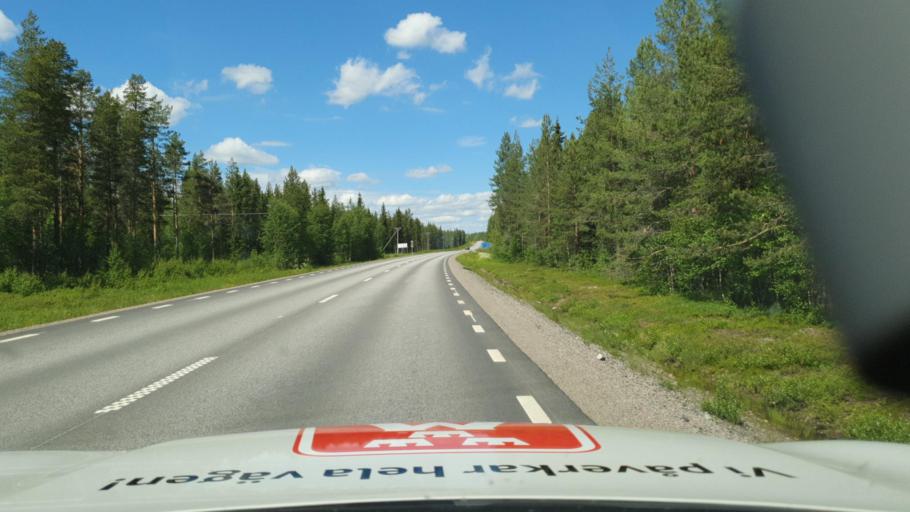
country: SE
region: Vaesterbotten
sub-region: Skelleftea Kommun
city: Langsele
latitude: 64.9458
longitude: 20.2721
